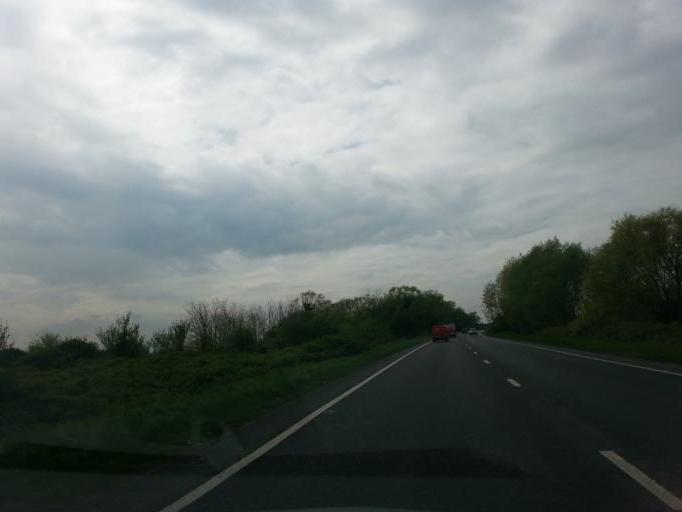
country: GB
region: England
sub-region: Cambridgeshire
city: Wisbech
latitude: 52.6468
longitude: 0.1669
